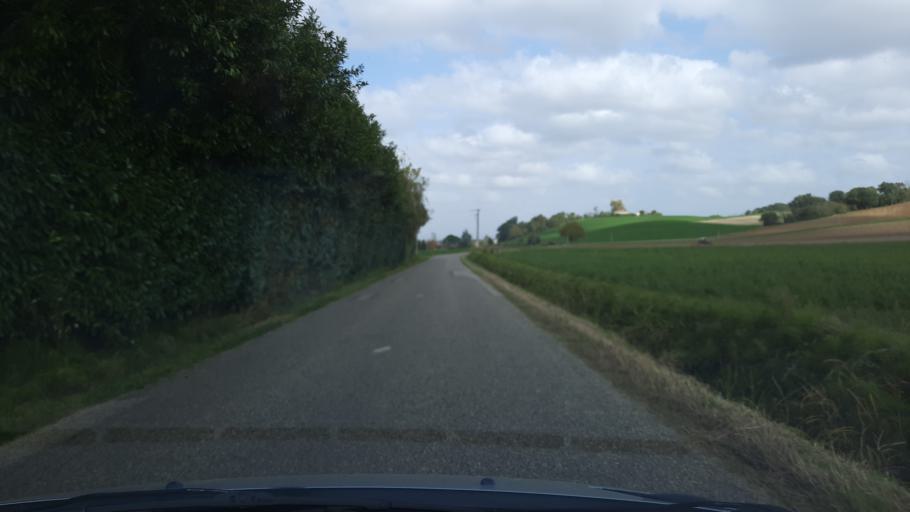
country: FR
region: Midi-Pyrenees
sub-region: Departement du Tarn-et-Garonne
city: Lafrancaise
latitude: 44.1813
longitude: 1.2795
